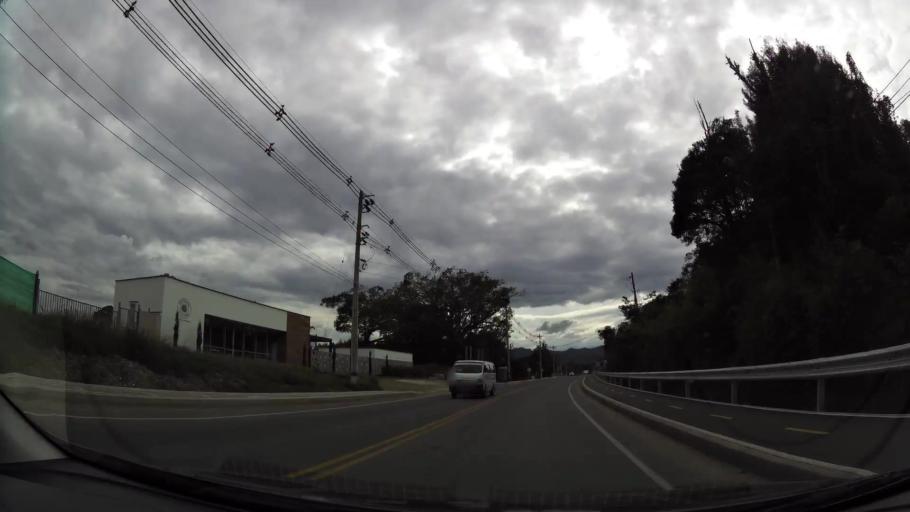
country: CO
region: Antioquia
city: Rionegro
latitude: 6.1482
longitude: -75.4204
